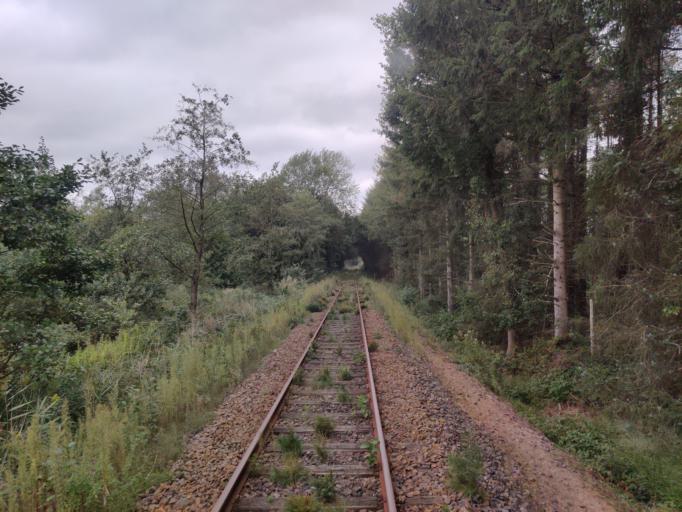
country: DE
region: Lower Saxony
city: Basdahl
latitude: 53.4176
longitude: 9.0152
